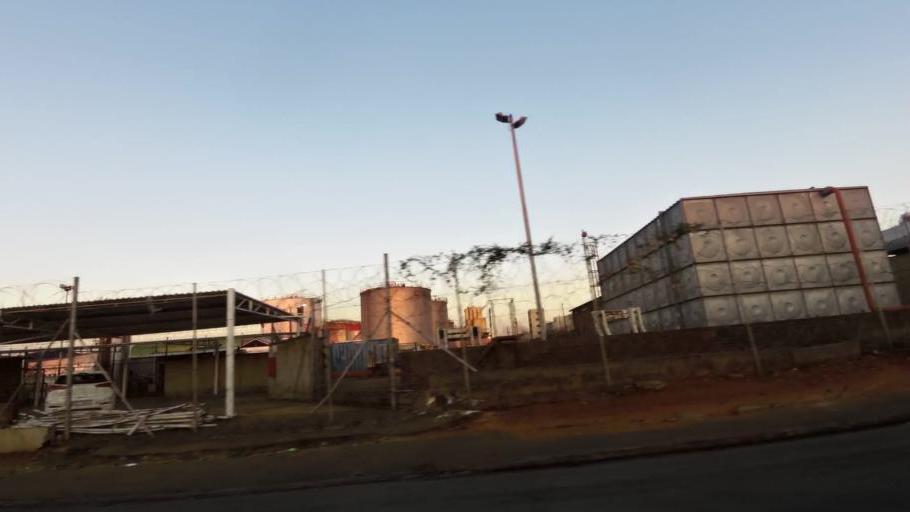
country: ZA
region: Gauteng
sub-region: City of Johannesburg Metropolitan Municipality
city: Johannesburg
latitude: -26.2006
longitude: 27.9720
